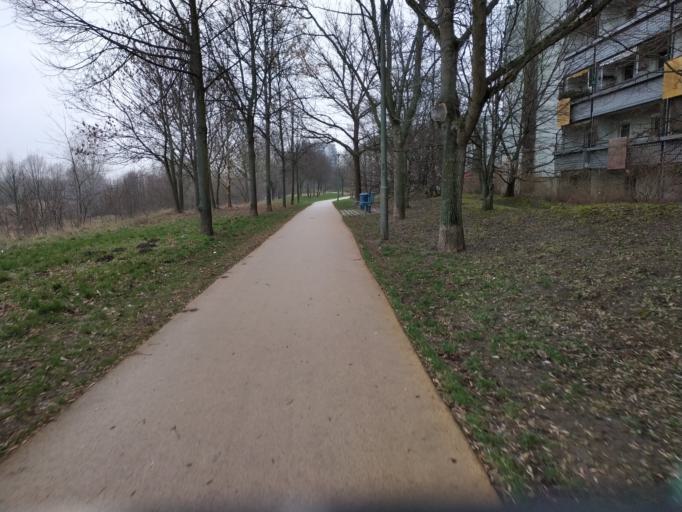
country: DE
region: Berlin
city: Kaulsdorf
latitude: 52.5360
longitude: 13.5872
